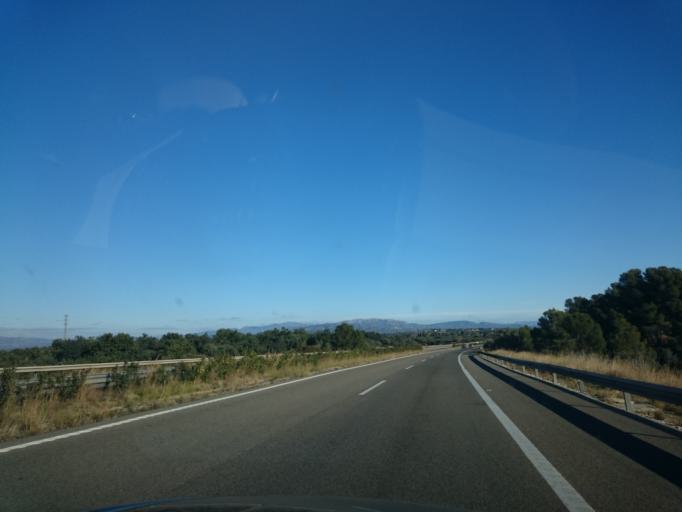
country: ES
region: Catalonia
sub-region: Provincia de Tarragona
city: Masdenverge
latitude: 40.6880
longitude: 0.5277
